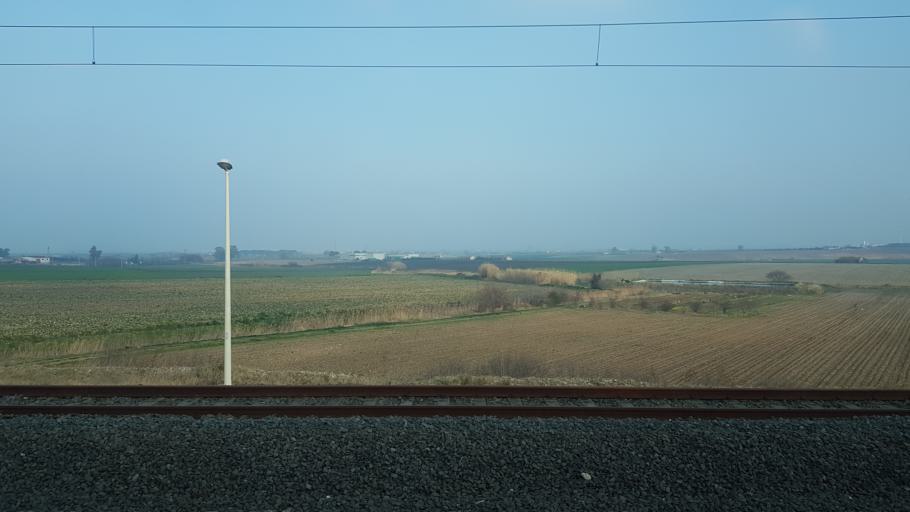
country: IT
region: Apulia
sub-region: Provincia di Foggia
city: Lesina
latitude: 41.8519
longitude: 15.2959
